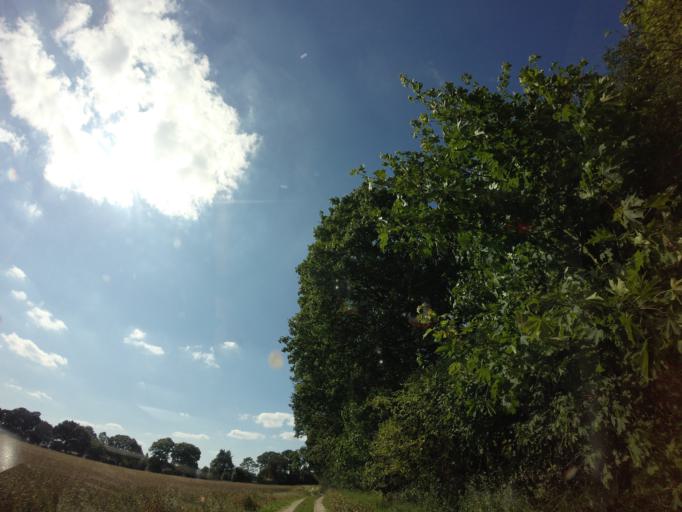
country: PL
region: West Pomeranian Voivodeship
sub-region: Powiat choszczenski
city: Recz
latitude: 53.2644
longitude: 15.6265
